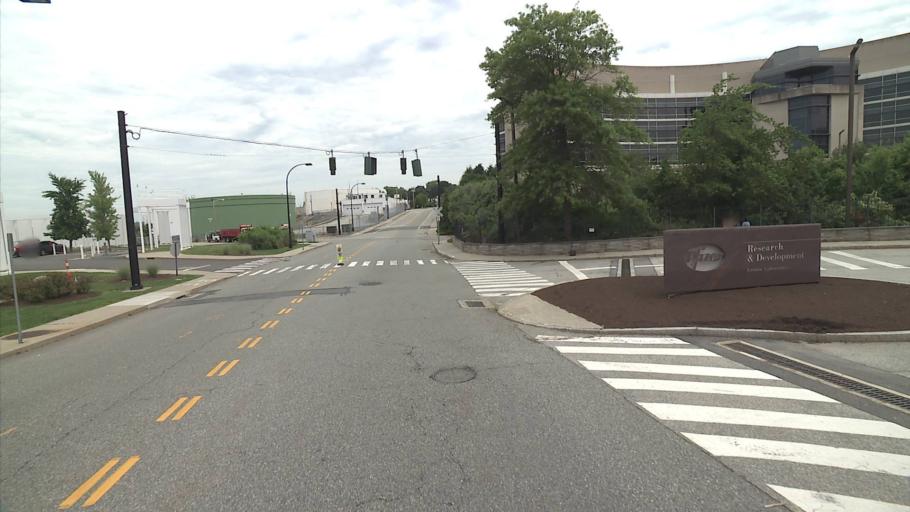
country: US
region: Connecticut
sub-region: New London County
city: Groton
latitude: 41.3342
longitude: -72.0764
